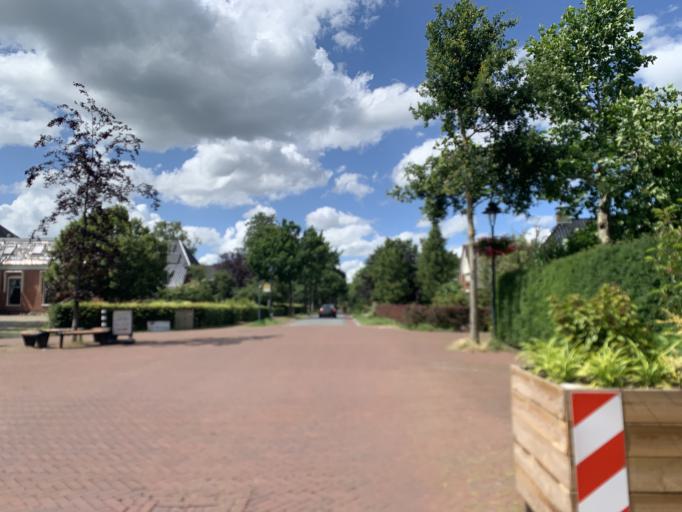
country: NL
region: Groningen
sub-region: Gemeente Haren
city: Haren
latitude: 53.1583
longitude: 6.6404
